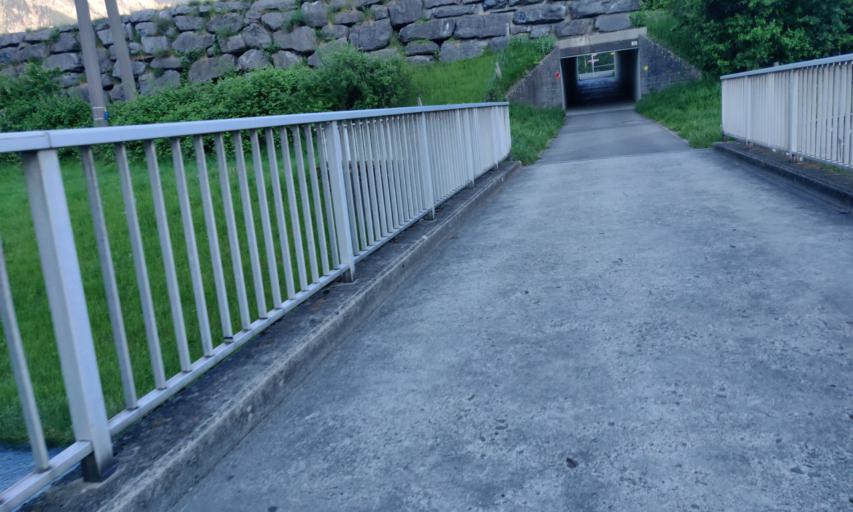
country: LI
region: Balzers
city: Balzers
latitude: 47.0708
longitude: 9.4810
